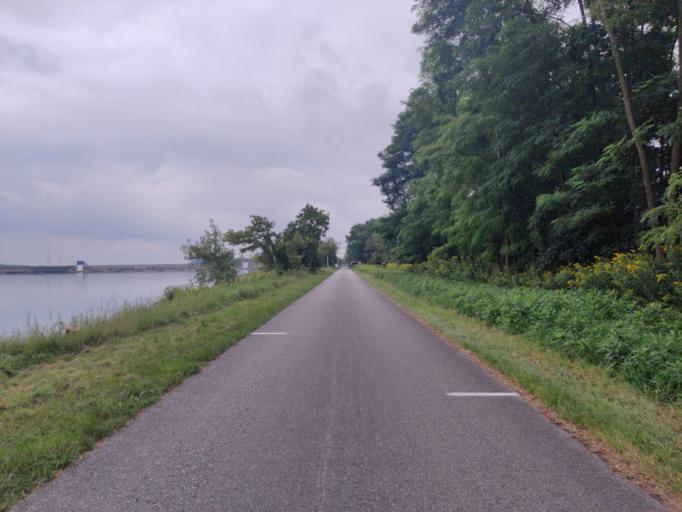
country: AT
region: Lower Austria
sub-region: Politischer Bezirk Tulln
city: Fels am Wagram
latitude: 48.3762
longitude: 15.8493
